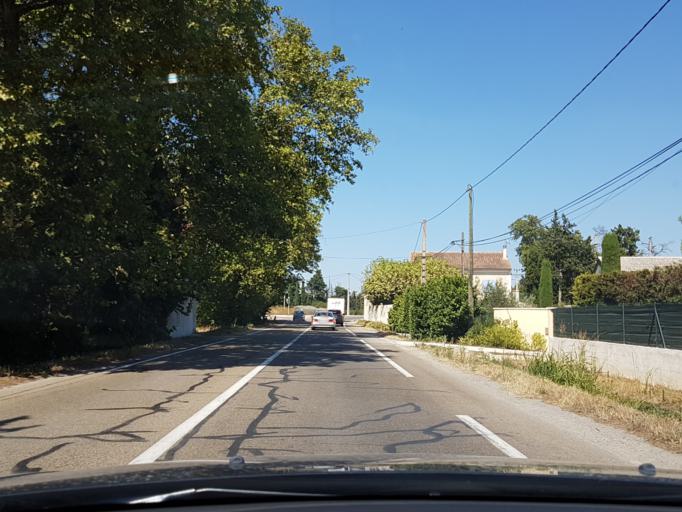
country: FR
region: Provence-Alpes-Cote d'Azur
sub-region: Departement des Bouches-du-Rhone
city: Chateaurenard
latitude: 43.8761
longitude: 4.8346
